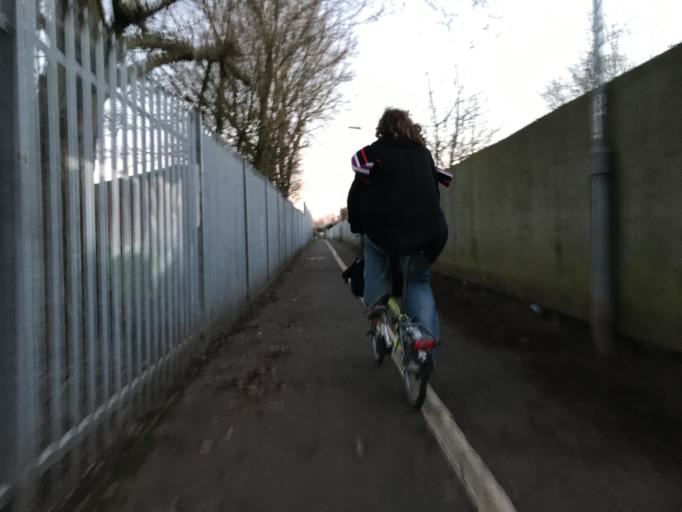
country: GB
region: England
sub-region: Lincolnshire
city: Holton le Clay
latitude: 53.5251
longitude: -0.0640
